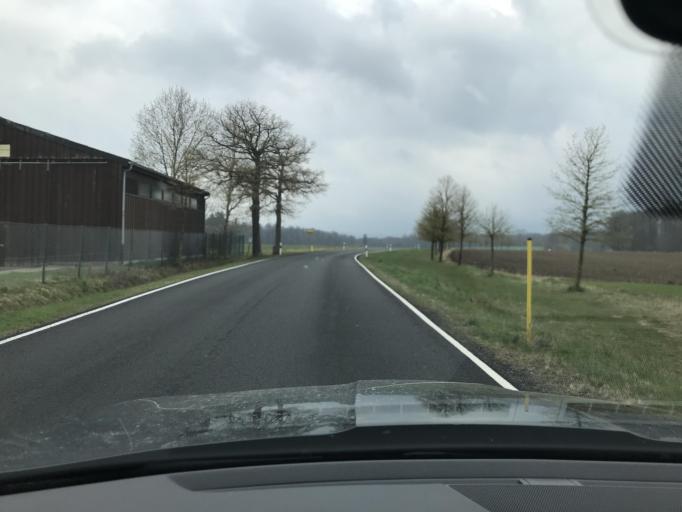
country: DE
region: Saxony-Anhalt
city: Harzgerode
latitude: 51.6521
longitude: 11.1382
